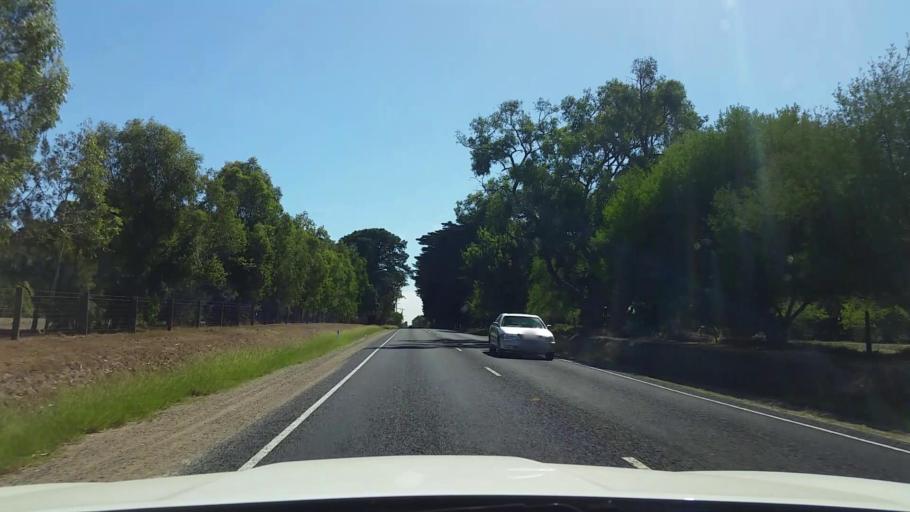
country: AU
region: Victoria
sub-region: Mornington Peninsula
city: Hastings
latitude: -38.2767
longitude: 145.1456
